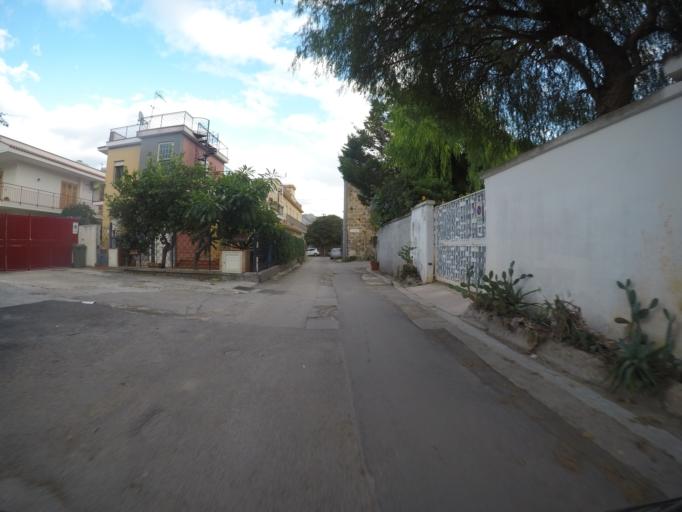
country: IT
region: Sicily
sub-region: Palermo
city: Isola delle Femmine
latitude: 38.2015
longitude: 13.3125
